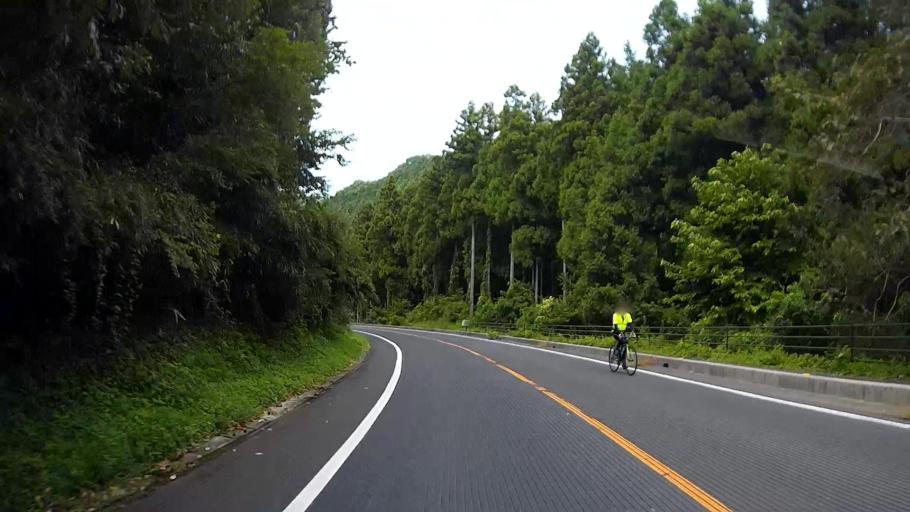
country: JP
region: Tokyo
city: Ome
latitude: 35.8586
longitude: 139.2133
